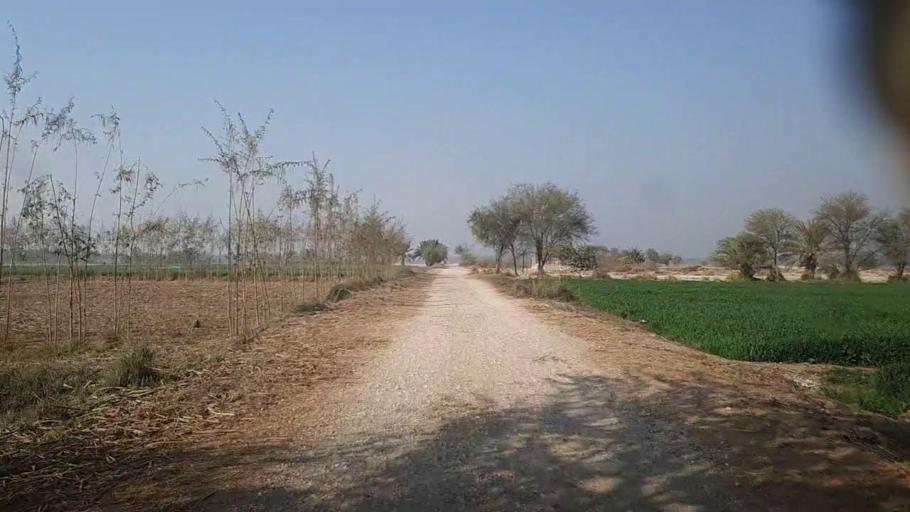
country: PK
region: Sindh
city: Karaundi
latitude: 26.8474
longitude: 68.3973
